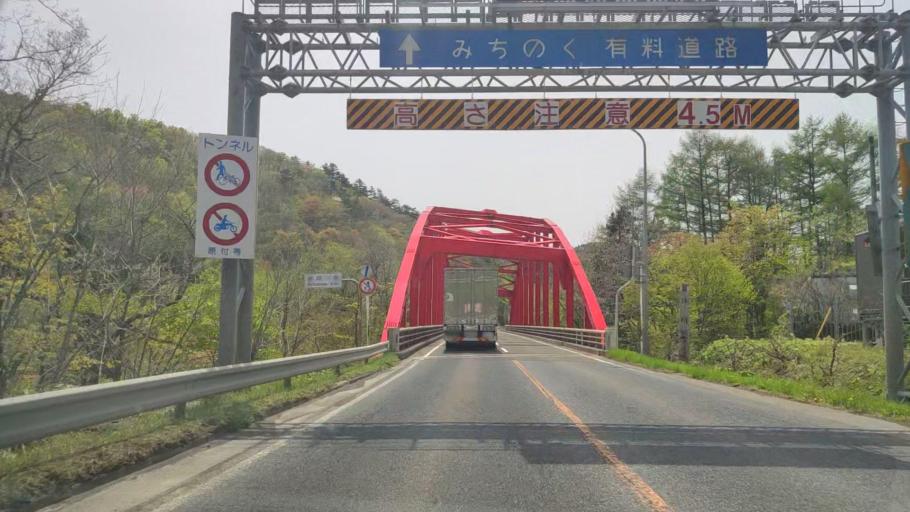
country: JP
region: Aomori
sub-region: Misawa Shi
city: Inuotose
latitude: 40.7902
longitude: 141.0861
